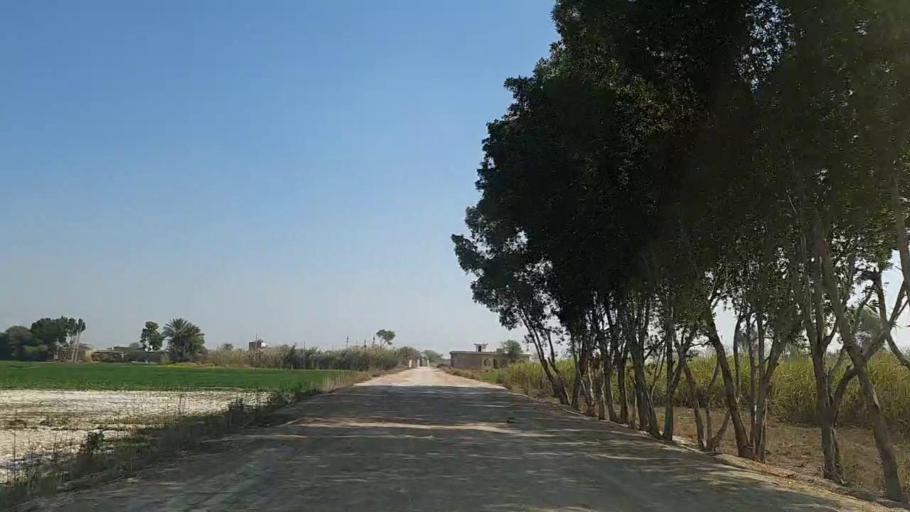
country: PK
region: Sindh
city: Daur
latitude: 26.5229
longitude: 68.3166
